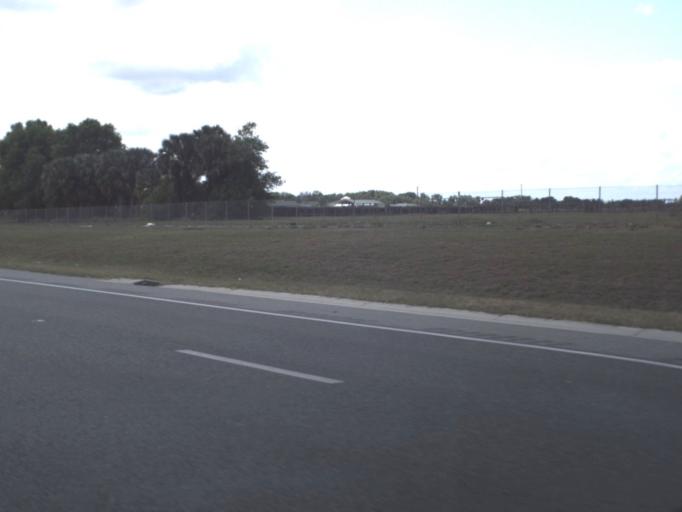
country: US
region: Florida
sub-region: Orange County
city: Paradise Heights
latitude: 28.6430
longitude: -81.5435
